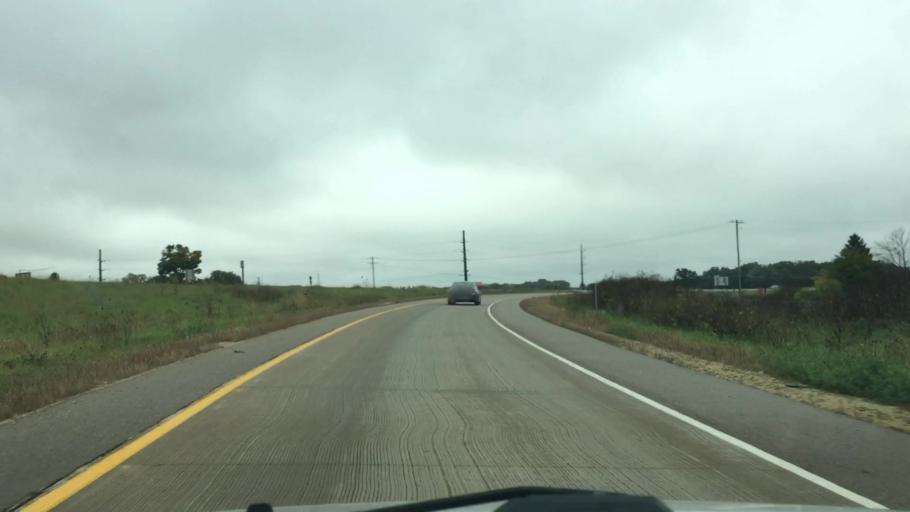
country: US
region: Wisconsin
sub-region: Rock County
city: Milton
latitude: 42.7674
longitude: -88.9248
